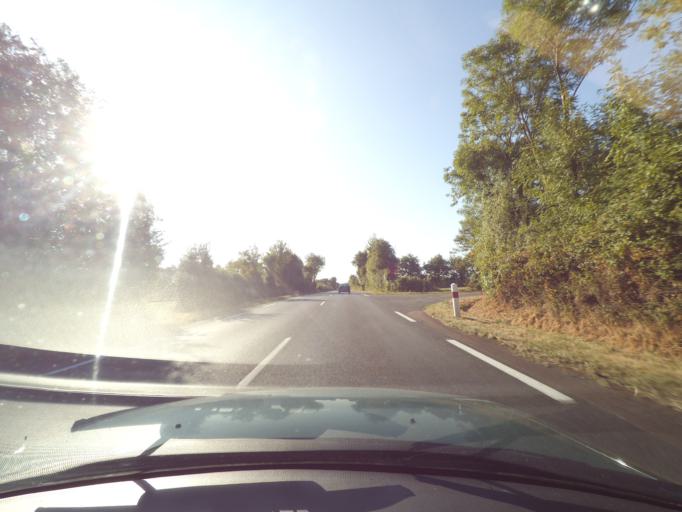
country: FR
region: Poitou-Charentes
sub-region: Departement des Deux-Sevres
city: Boisme
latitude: 46.8189
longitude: -0.4056
